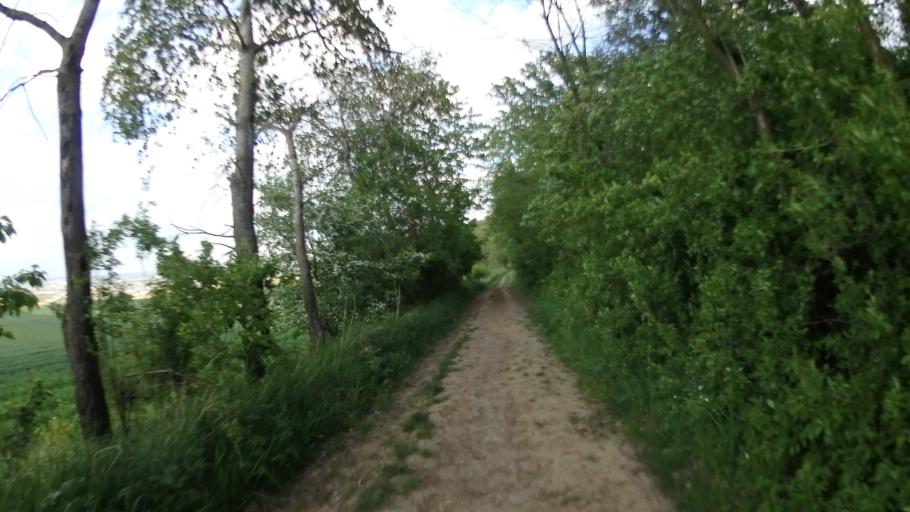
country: CZ
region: South Moravian
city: Moravany
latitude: 49.1350
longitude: 16.5714
